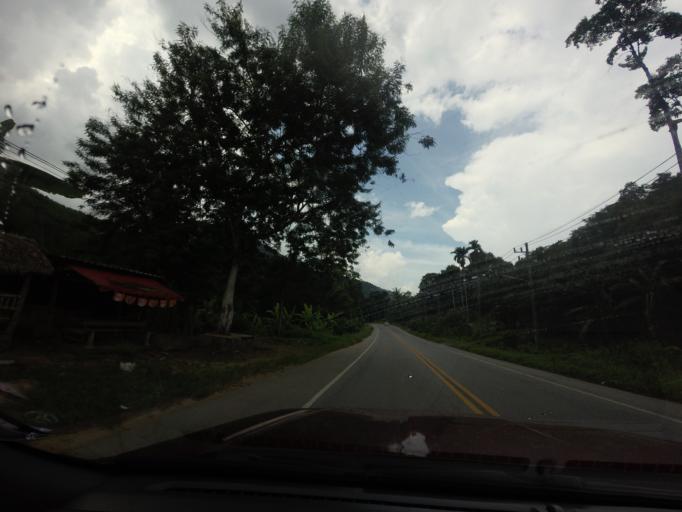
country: TH
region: Yala
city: Than To
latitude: 6.2356
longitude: 101.1830
